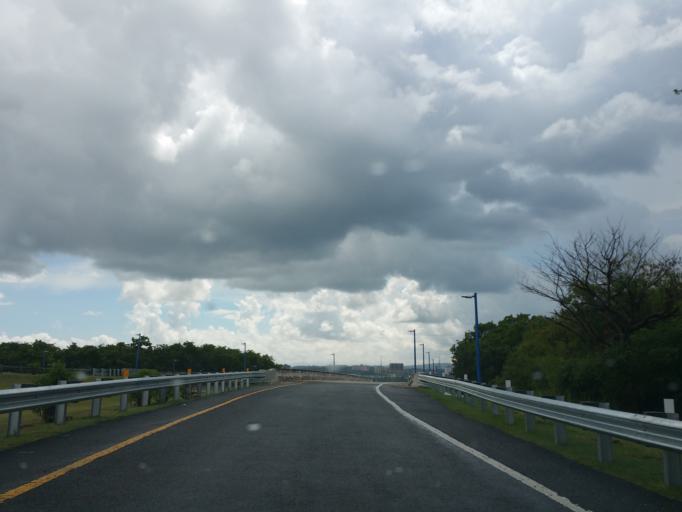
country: PR
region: Trujillo Alto
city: Trujillo Alto
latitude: 18.4351
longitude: -66.0219
